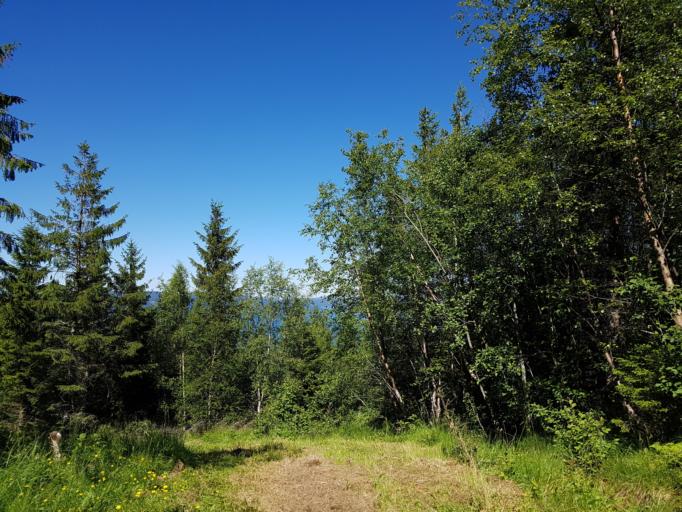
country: NO
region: Sor-Trondelag
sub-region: Melhus
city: Melhus
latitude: 63.4401
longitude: 10.2095
